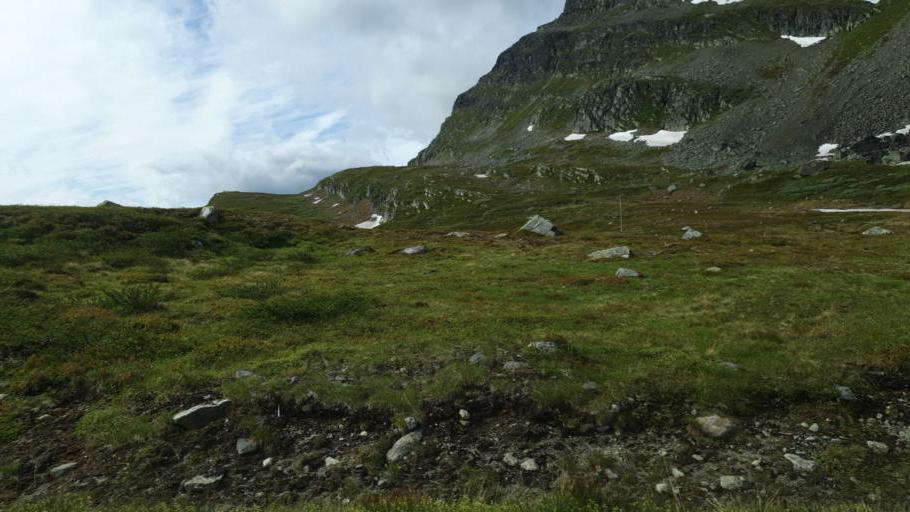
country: NO
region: Oppland
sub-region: Vestre Slidre
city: Slidre
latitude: 61.2991
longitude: 8.8125
